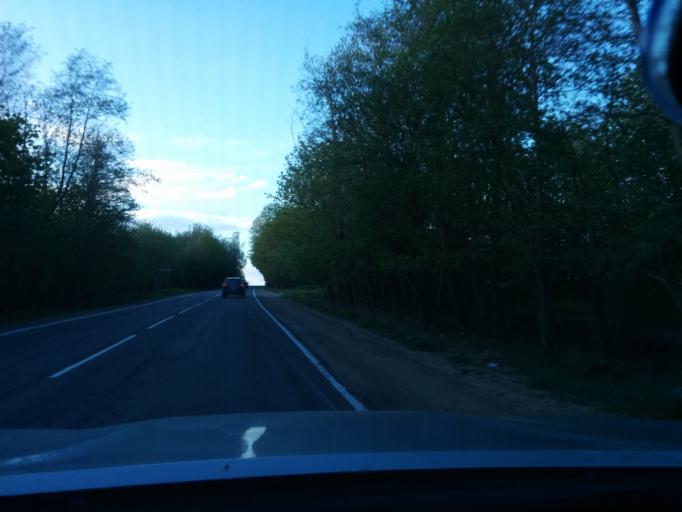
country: RU
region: Leningrad
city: Verkhniye Osel'ki
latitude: 60.2379
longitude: 30.4391
